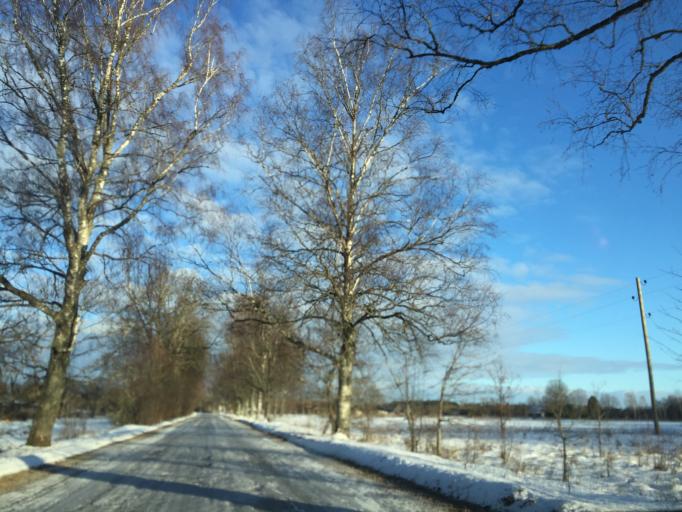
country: LV
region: Kegums
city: Kegums
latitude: 56.7414
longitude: 24.6662
